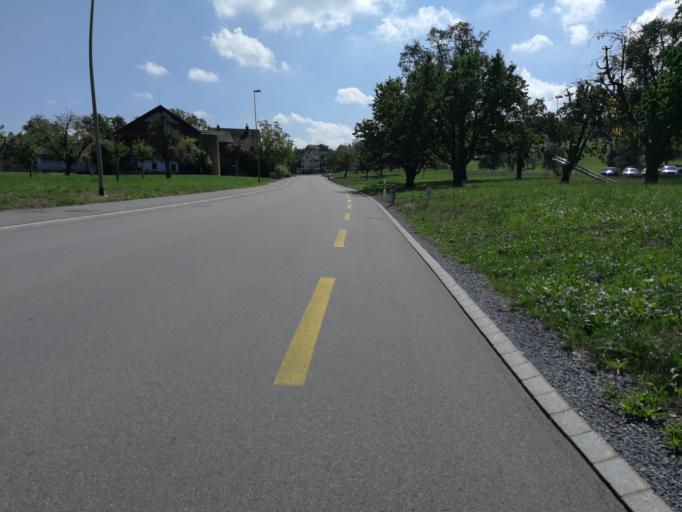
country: CH
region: Zurich
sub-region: Bezirk Horgen
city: Horgen / Allmend
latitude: 47.2502
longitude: 8.6185
